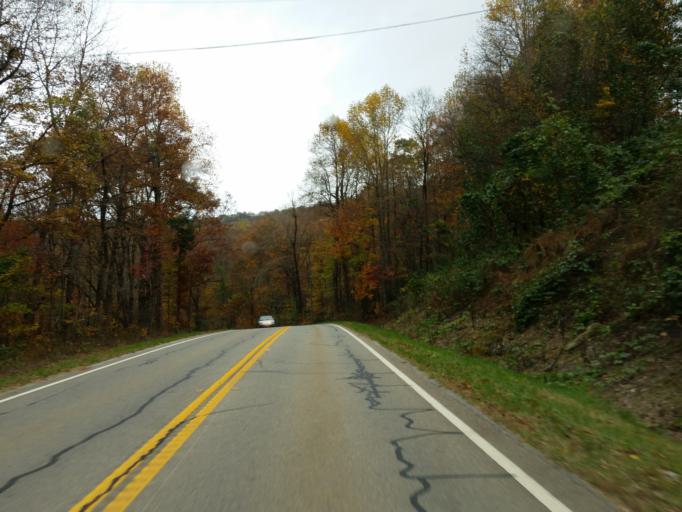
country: US
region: Georgia
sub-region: Pickens County
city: Jasper
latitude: 34.5428
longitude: -84.3677
